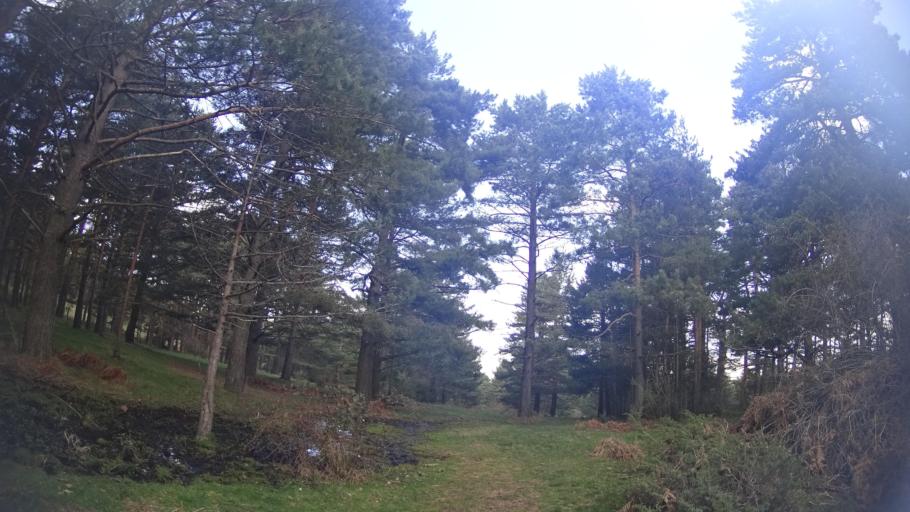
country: ES
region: Madrid
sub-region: Provincia de Madrid
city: Canencia
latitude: 40.8744
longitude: -3.7686
